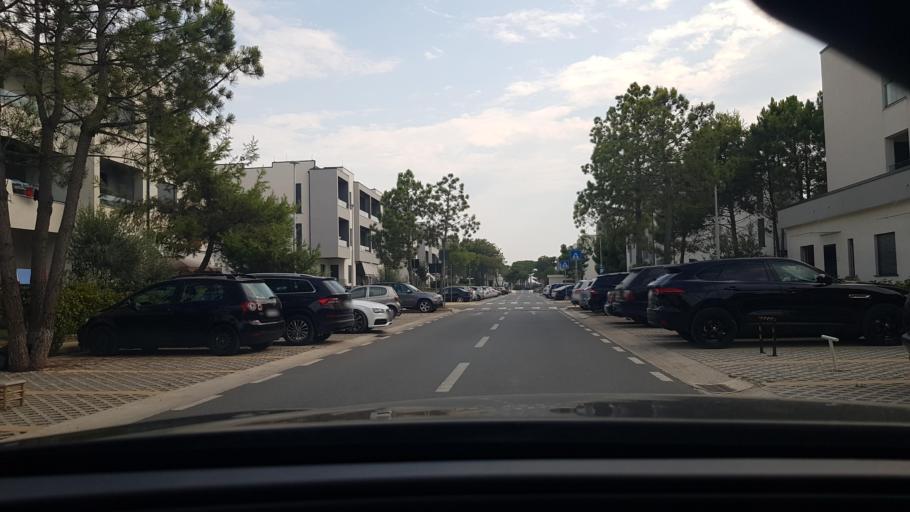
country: AL
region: Durres
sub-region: Rrethi i Durresit
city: Katundi i Ri
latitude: 41.4905
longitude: 19.5130
